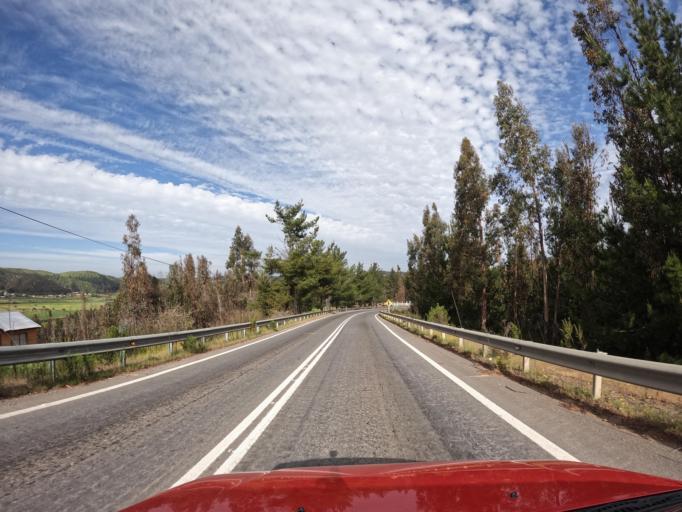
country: CL
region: O'Higgins
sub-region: Provincia de Colchagua
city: Santa Cruz
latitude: -34.2963
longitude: -71.8032
